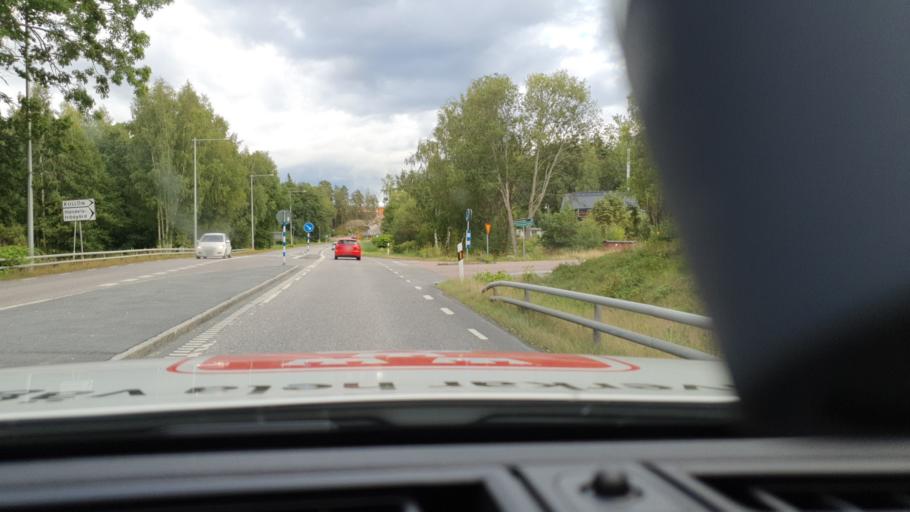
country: SE
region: Stockholm
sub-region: Vaxholms Kommun
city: Resaro
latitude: 59.4154
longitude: 18.3128
